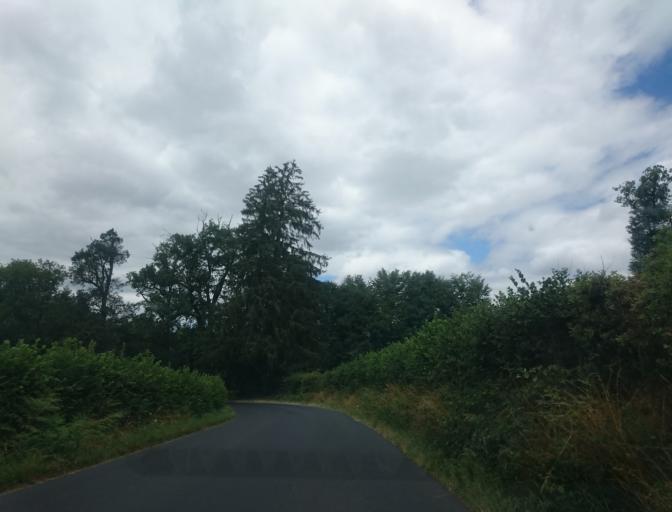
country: FR
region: Auvergne
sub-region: Departement du Cantal
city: Laroquebrou
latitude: 44.9529
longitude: 2.2003
